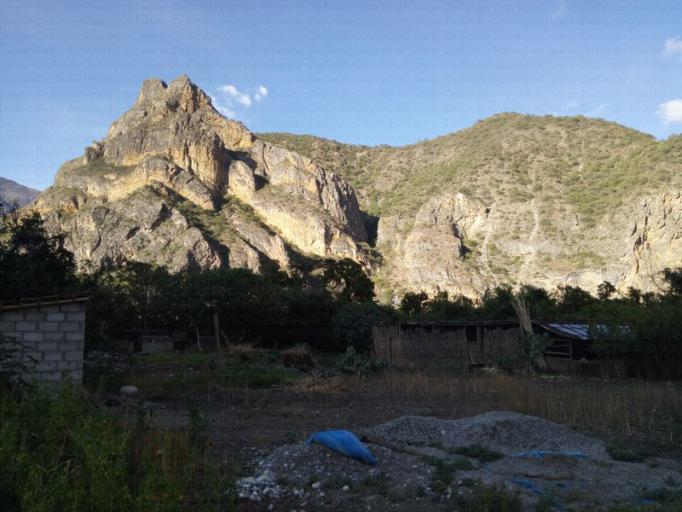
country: PE
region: Apurimac
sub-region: Provincia de Abancay
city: Pichirhua
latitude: -13.8491
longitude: -72.9788
